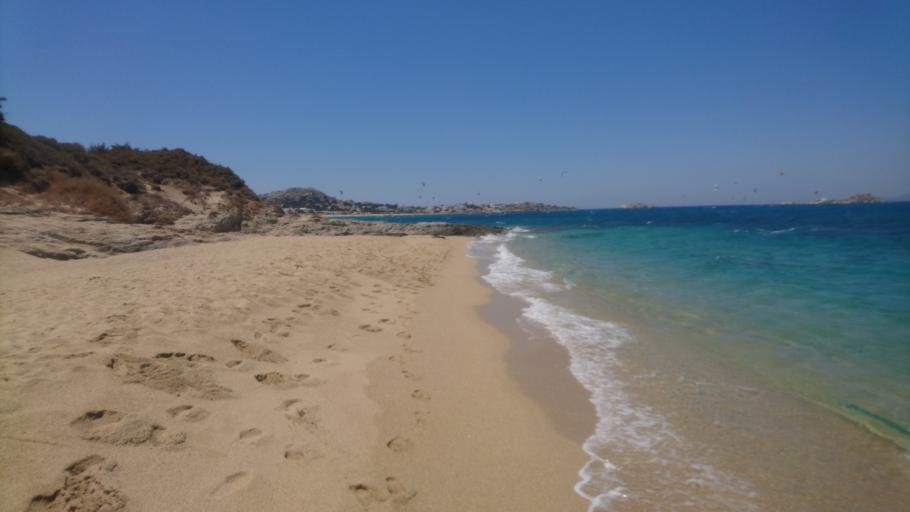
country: GR
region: South Aegean
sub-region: Nomos Kykladon
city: Naxos
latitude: 37.0323
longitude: 25.3731
